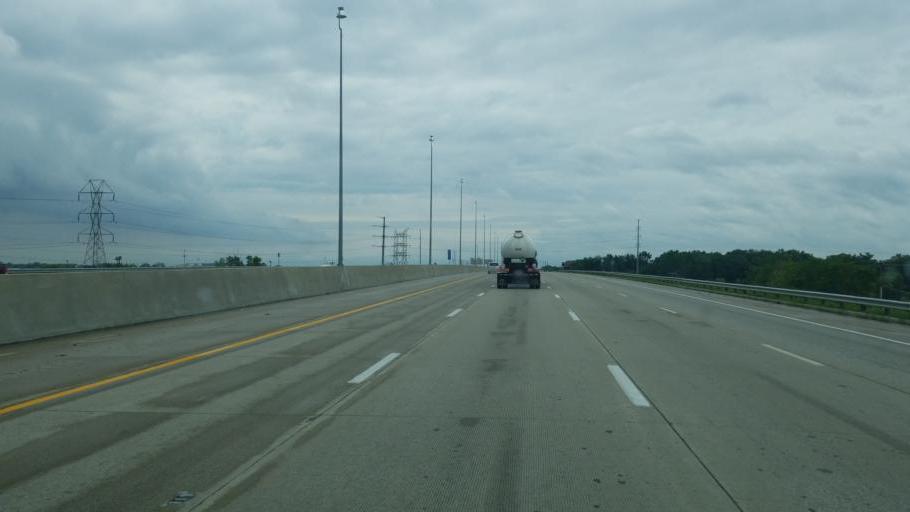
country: US
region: Ohio
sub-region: Franklin County
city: Lincoln Village
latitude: 39.9673
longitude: -83.1196
